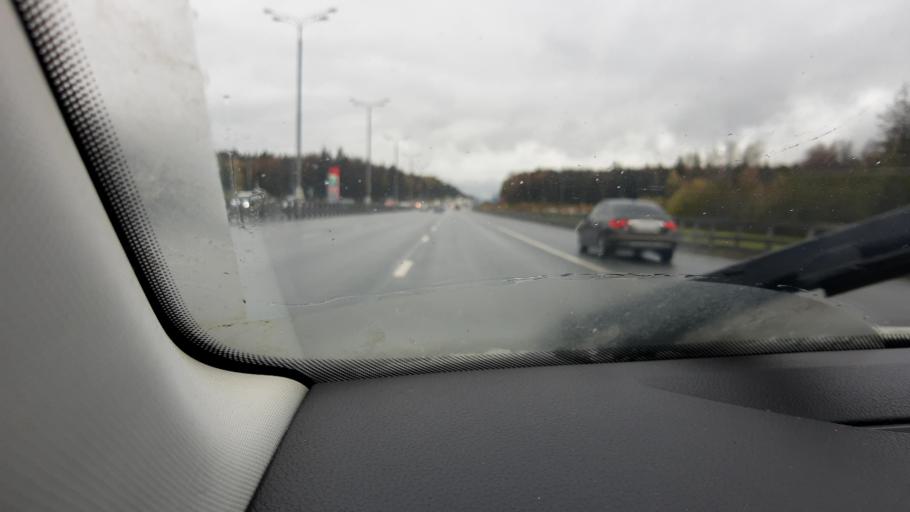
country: RU
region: Moskovskaya
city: Aprelevka
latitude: 55.5509
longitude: 37.1296
